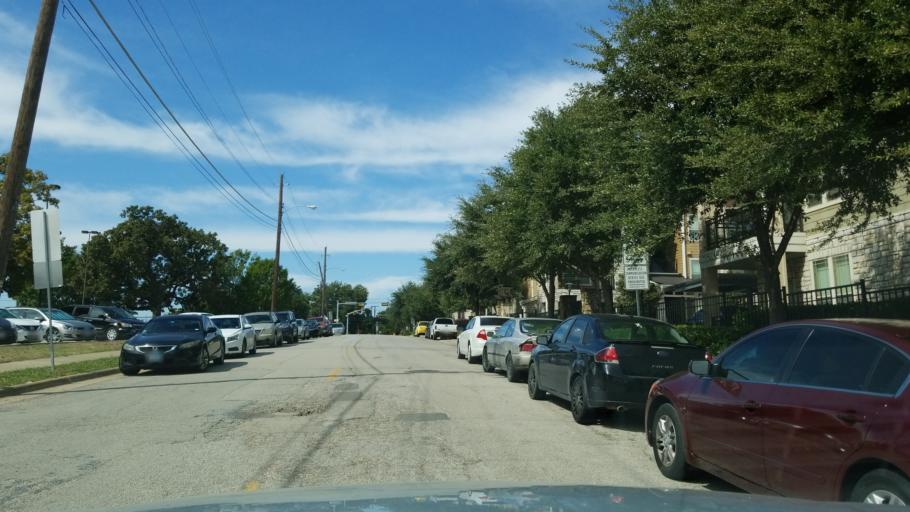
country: US
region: Texas
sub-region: Dallas County
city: Highland Park
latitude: 32.8069
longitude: -96.7311
